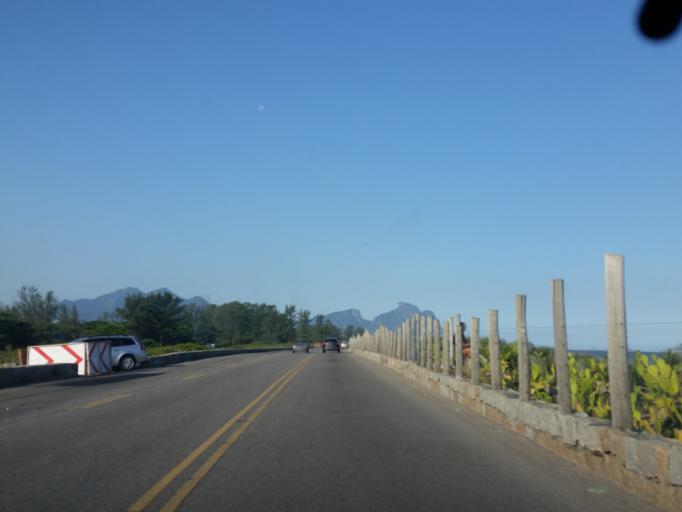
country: BR
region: Rio de Janeiro
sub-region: Nilopolis
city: Nilopolis
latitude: -23.0179
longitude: -43.4253
